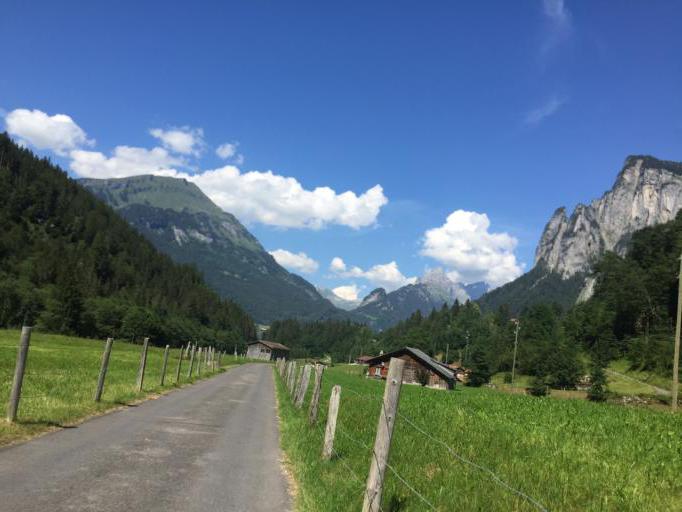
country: CH
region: Bern
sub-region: Interlaken-Oberhasli District
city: Meiringen
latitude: 46.6897
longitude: 8.2212
